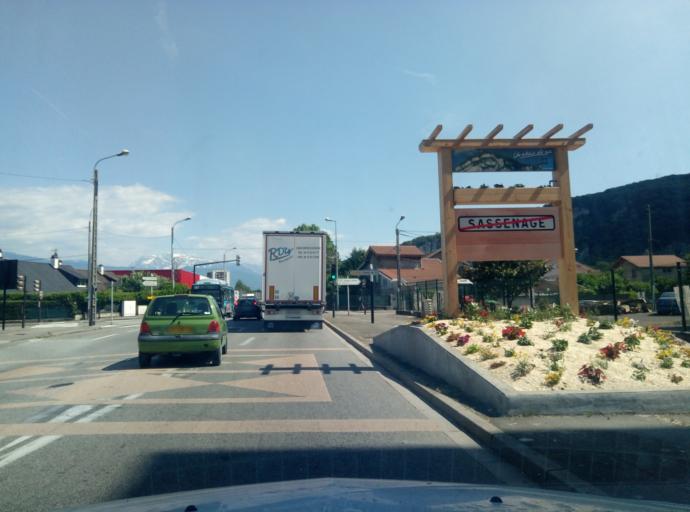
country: FR
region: Rhone-Alpes
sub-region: Departement de l'Isere
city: Sassenage
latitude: 45.1993
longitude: 5.6701
